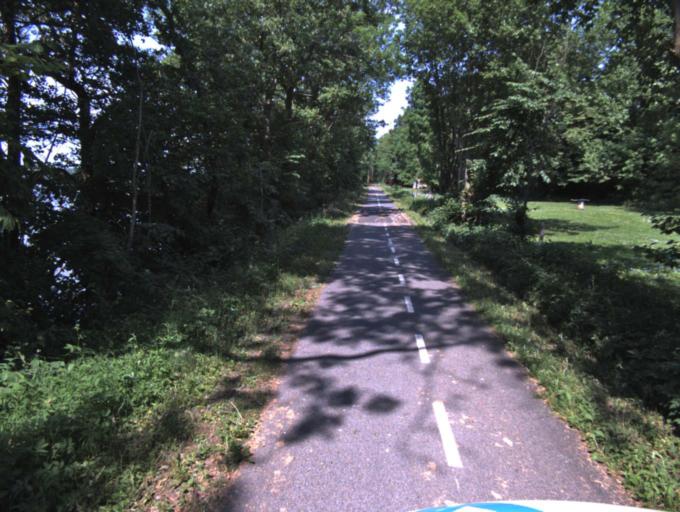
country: SE
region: Skane
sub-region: Kristianstads Kommun
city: Fjalkinge
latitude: 56.0895
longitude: 14.2330
